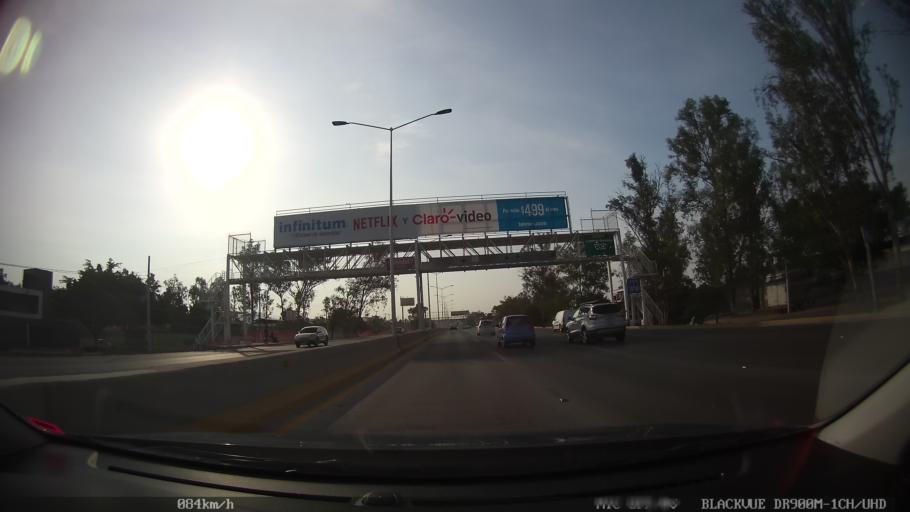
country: MX
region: Jalisco
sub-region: Zapopan
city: Zapopan
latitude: 20.7350
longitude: -103.3679
